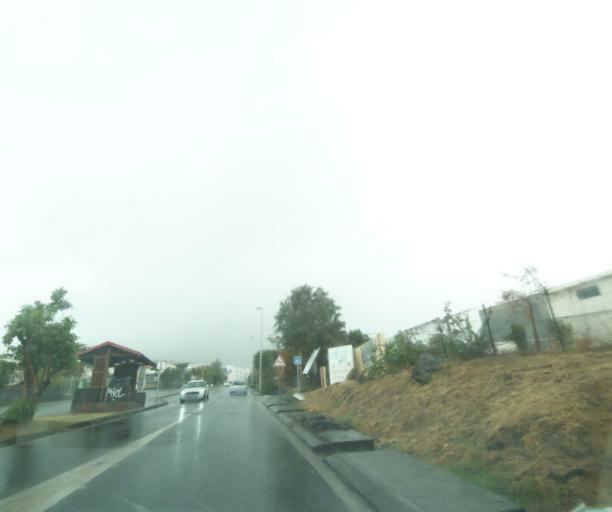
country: RE
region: Reunion
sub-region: Reunion
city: Saint-Paul
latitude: -21.0202
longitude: 55.2656
